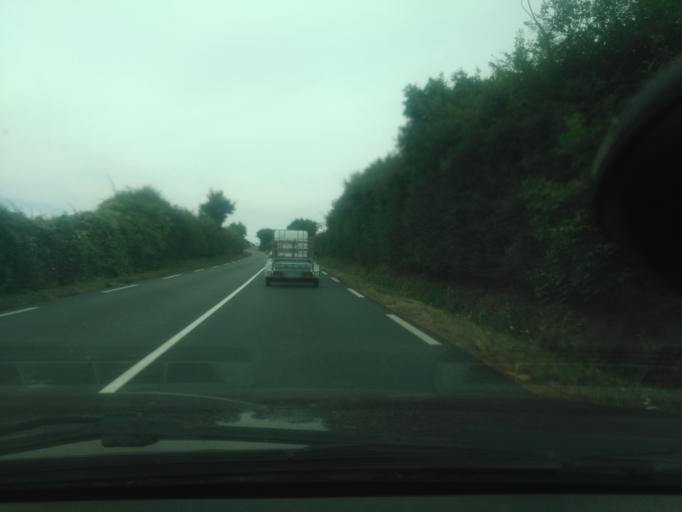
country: FR
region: Pays de la Loire
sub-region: Departement de la Vendee
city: Saint-Germain-de-Princay
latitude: 46.6775
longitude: -0.9792
